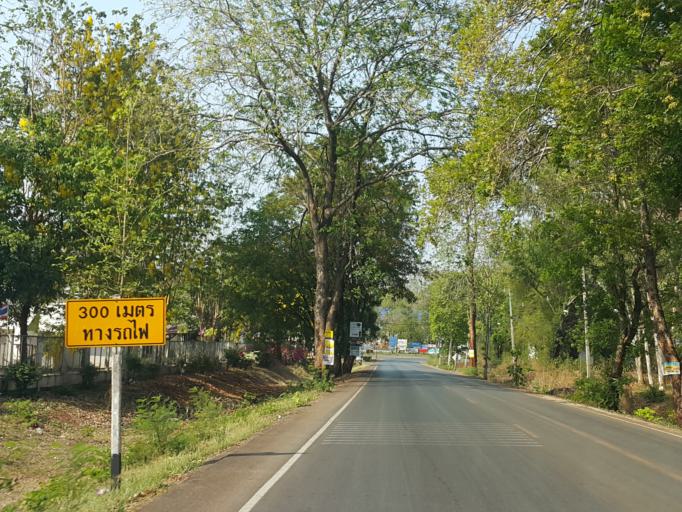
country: TH
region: Kanchanaburi
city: Sai Yok
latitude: 14.1195
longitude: 99.1451
